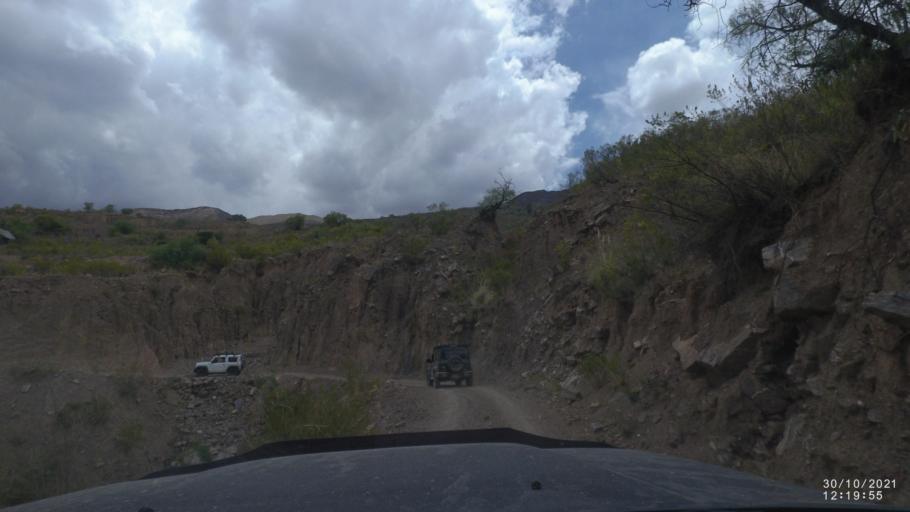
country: BO
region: Cochabamba
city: Colchani
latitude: -17.5691
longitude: -66.6317
